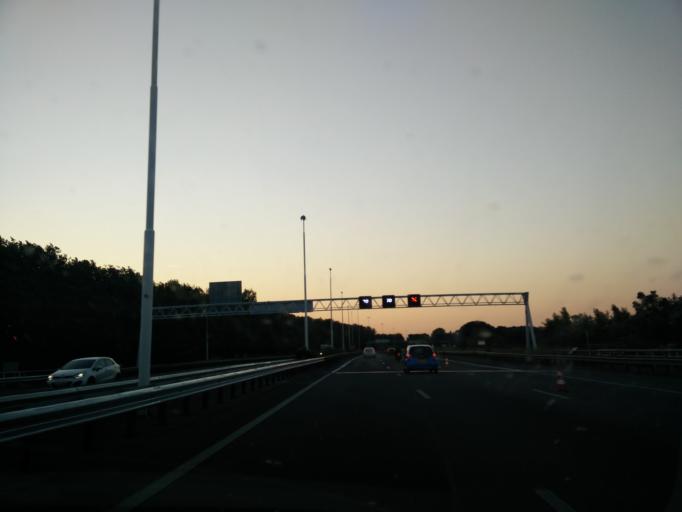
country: NL
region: South Holland
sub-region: Gemeente Strijen
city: Strijen
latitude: 51.7214
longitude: 4.6343
